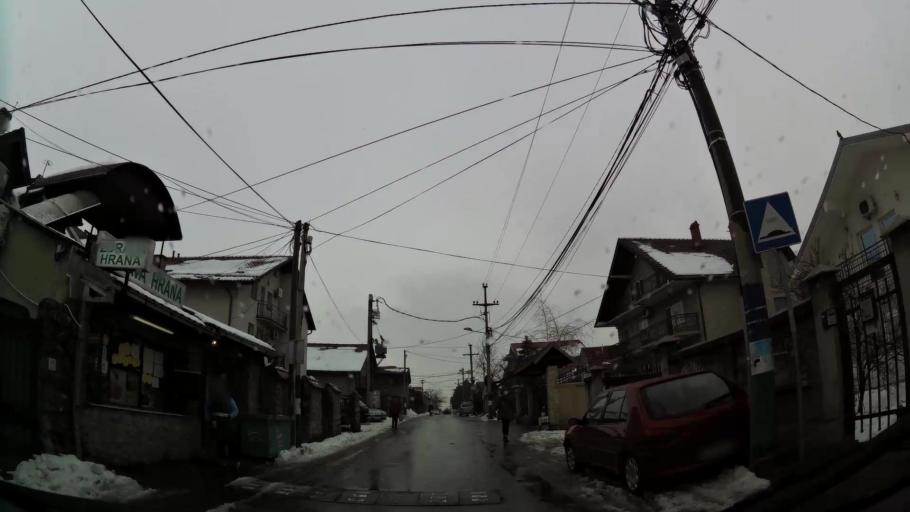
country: RS
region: Central Serbia
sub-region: Belgrade
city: Zemun
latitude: 44.8442
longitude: 20.3660
